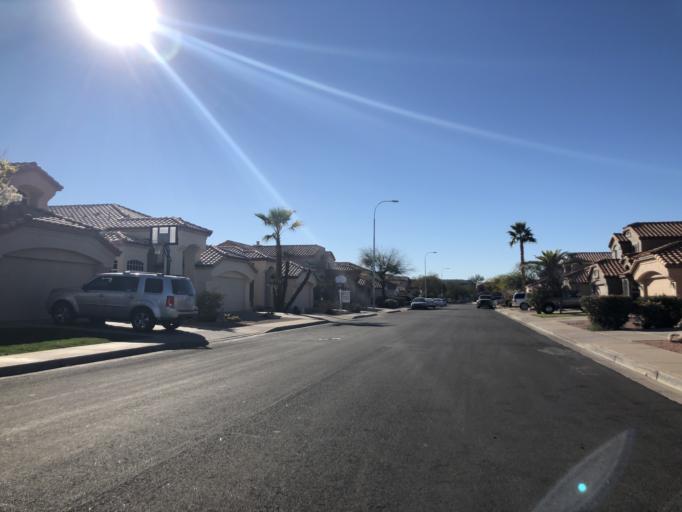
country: US
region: Arizona
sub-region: Maricopa County
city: Guadalupe
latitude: 33.3114
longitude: -111.9253
